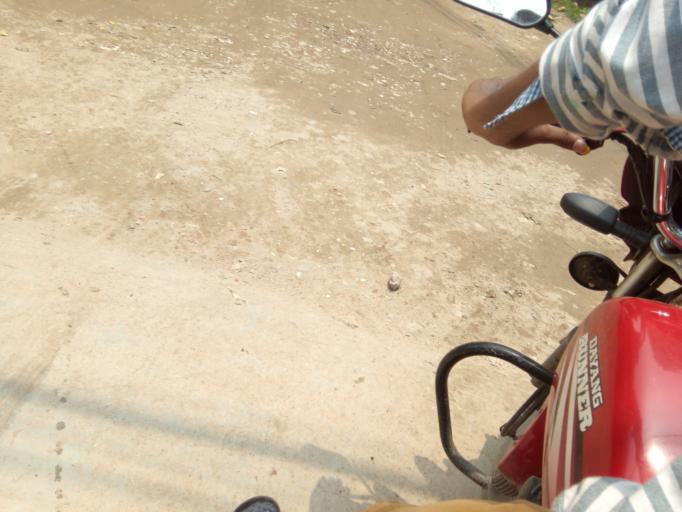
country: BD
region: Dhaka
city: Paltan
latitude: 23.7607
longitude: 90.4384
